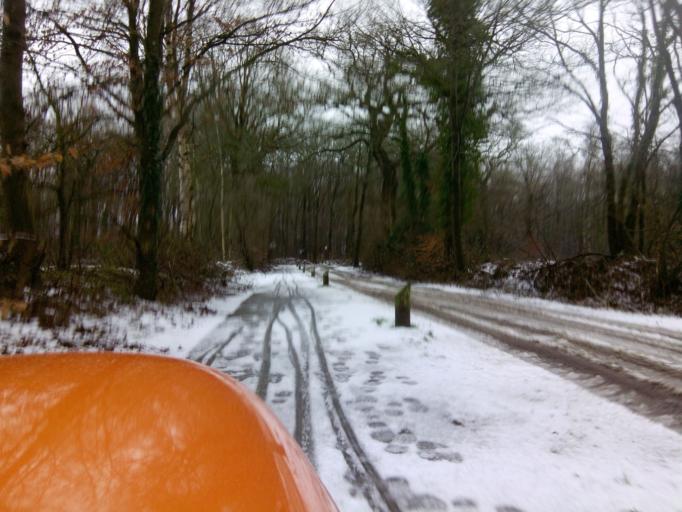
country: NL
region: Gelderland
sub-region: Gemeente Putten
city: Putten
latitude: 52.2256
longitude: 5.5595
